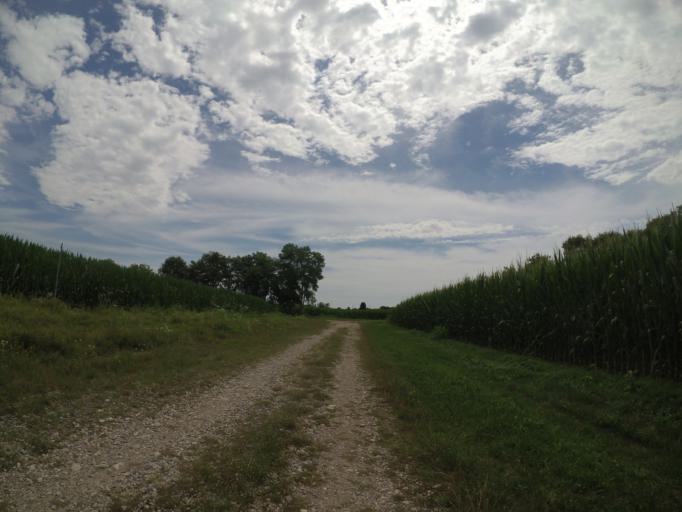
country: IT
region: Friuli Venezia Giulia
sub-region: Provincia di Udine
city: Bertiolo
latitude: 45.9699
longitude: 13.0599
